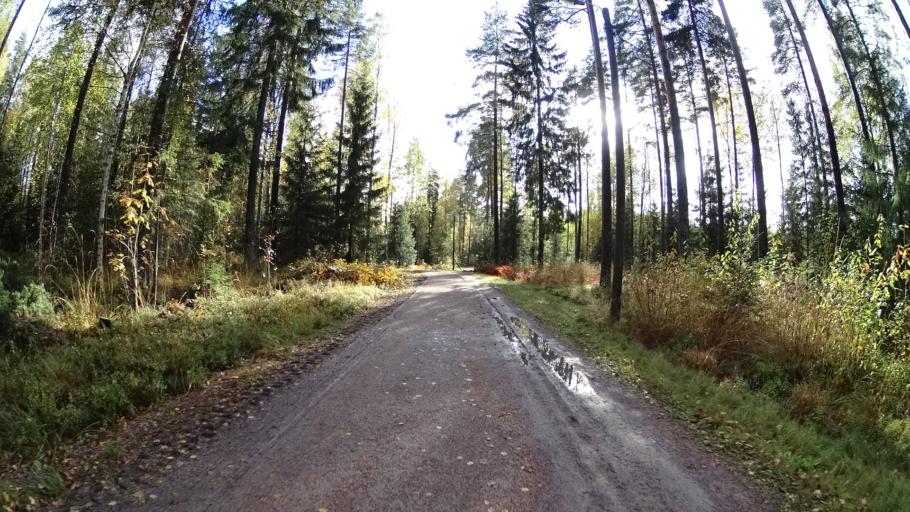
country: FI
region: Uusimaa
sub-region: Helsinki
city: Kilo
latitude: 60.3023
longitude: 24.8096
